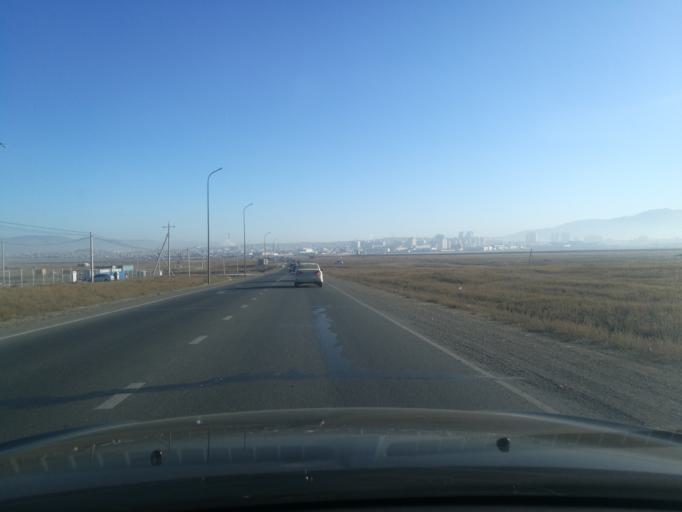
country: MN
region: Ulaanbaatar
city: Ulaanbaatar
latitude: 47.8496
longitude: 106.7389
